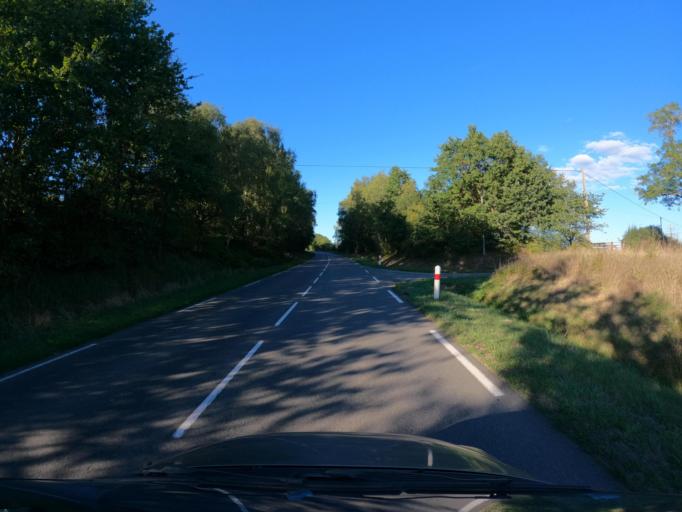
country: FR
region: Bourgogne
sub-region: Departement de Saone-et-Loire
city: Montchanin
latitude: 46.7379
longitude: 4.4446
